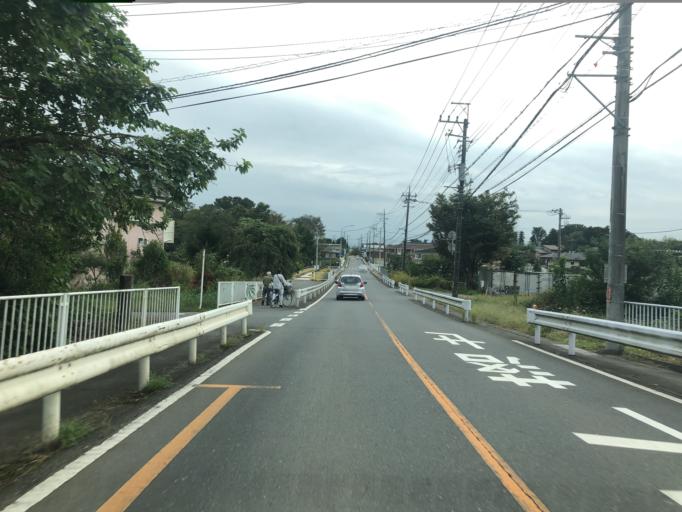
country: JP
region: Saitama
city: Fukiage-fujimi
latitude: 36.0542
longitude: 139.3962
